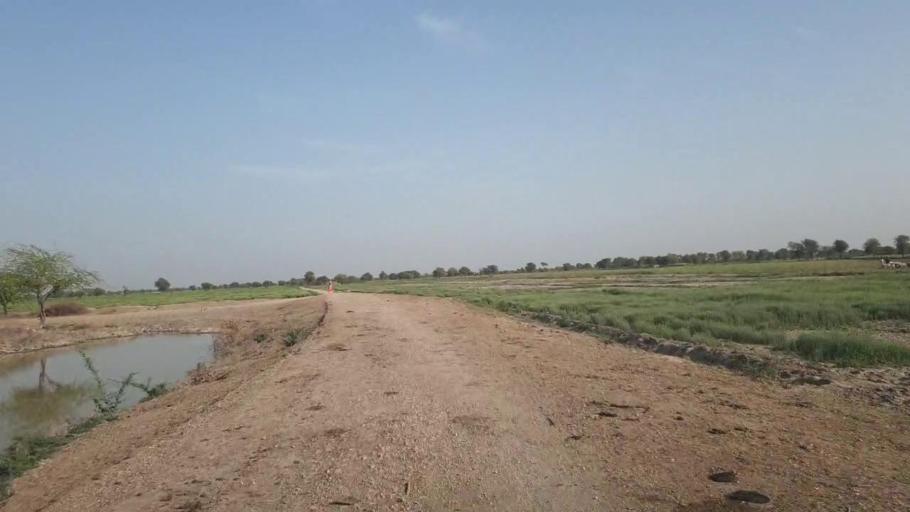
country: PK
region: Sindh
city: Dhoro Naro
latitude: 25.4710
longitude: 69.5748
